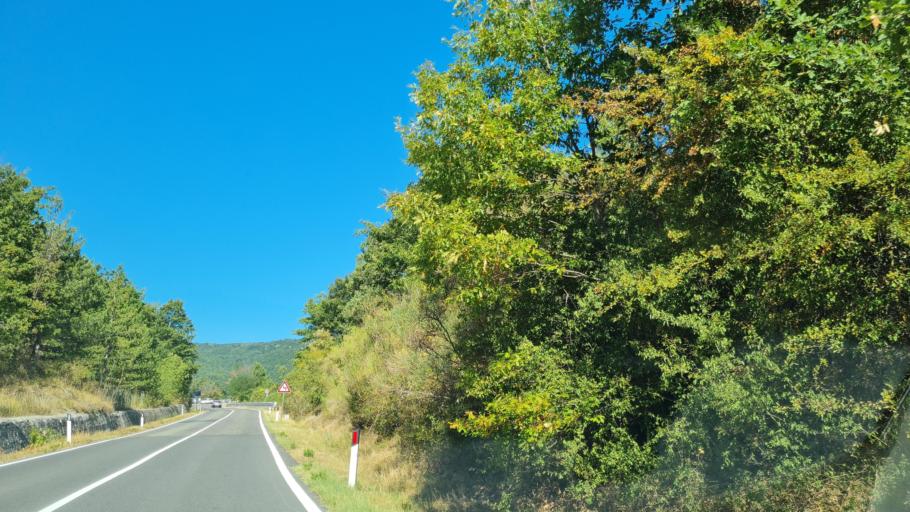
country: IT
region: Tuscany
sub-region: Provincia di Siena
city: Abbadia San Salvatore
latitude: 42.9208
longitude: 11.6977
